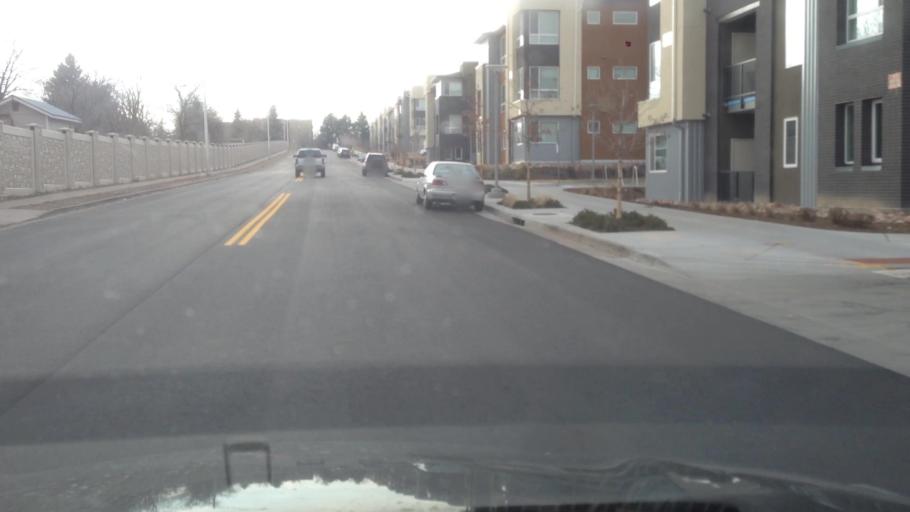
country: US
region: Colorado
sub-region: Adams County
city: Aurora
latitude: 39.6704
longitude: -104.8241
